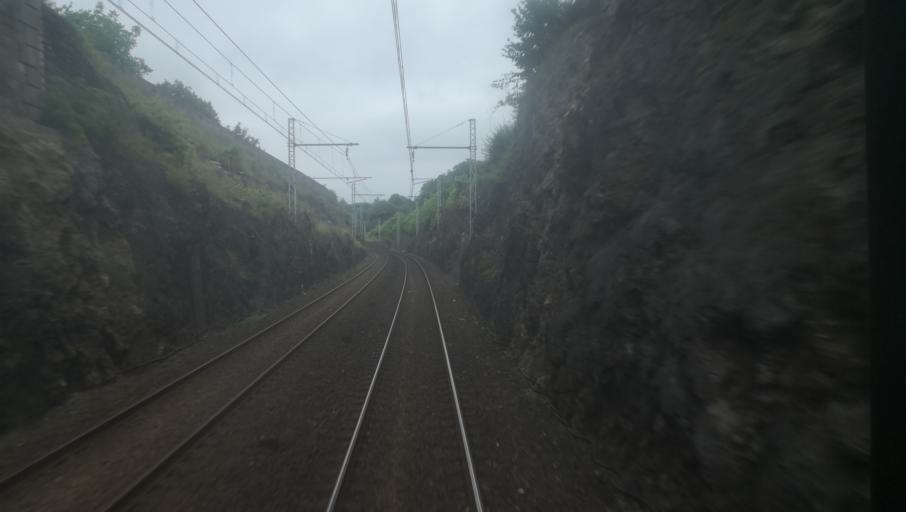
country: FR
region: Centre
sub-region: Departement de l'Indre
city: Saint-Marcel
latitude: 46.6240
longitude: 1.5045
